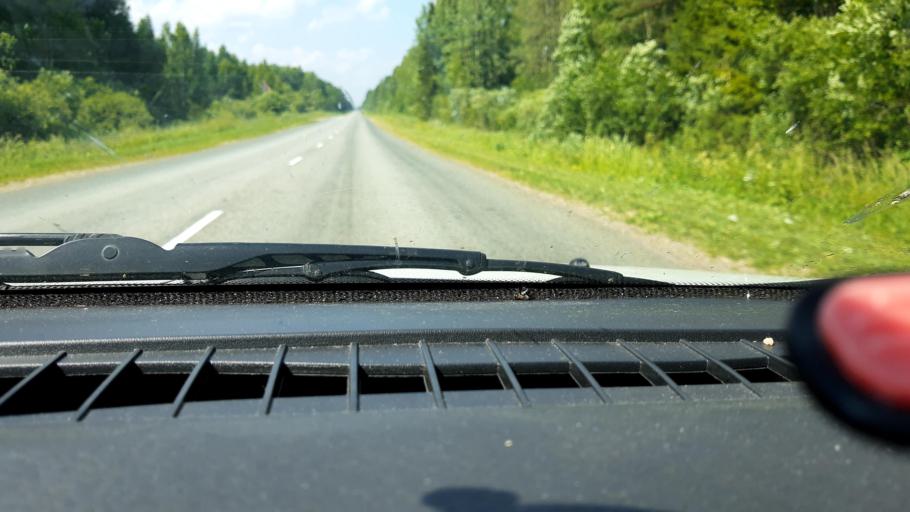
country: RU
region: Nizjnij Novgorod
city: Sharanga
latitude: 57.2254
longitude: 46.4978
